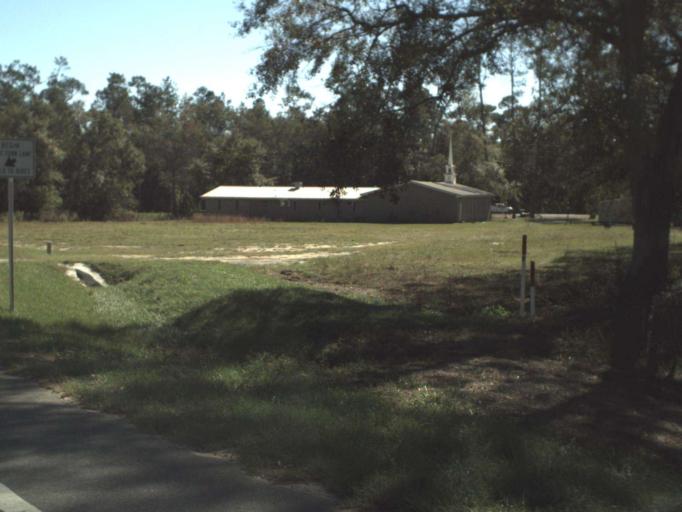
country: US
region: Florida
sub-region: Okaloosa County
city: Crestview
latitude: 30.7514
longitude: -86.6385
